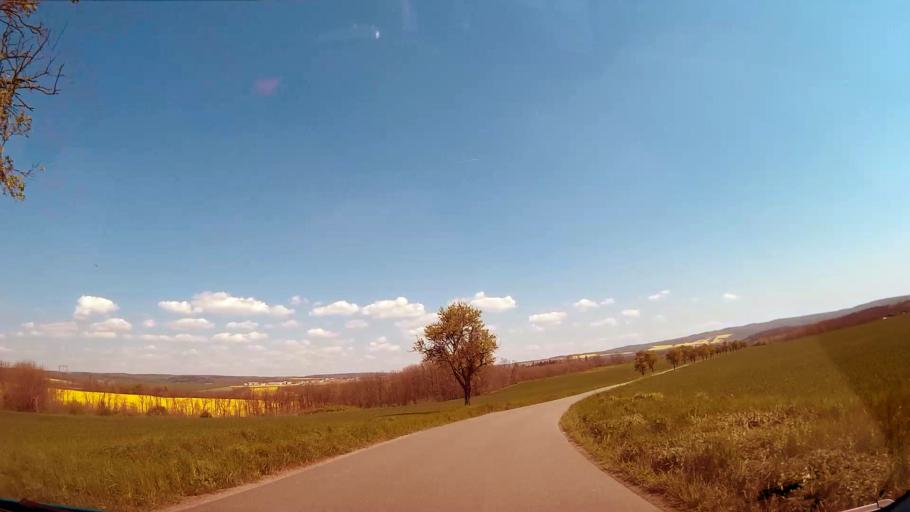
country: CZ
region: South Moravian
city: Moravsky Krumlov
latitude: 49.0760
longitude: 16.3102
